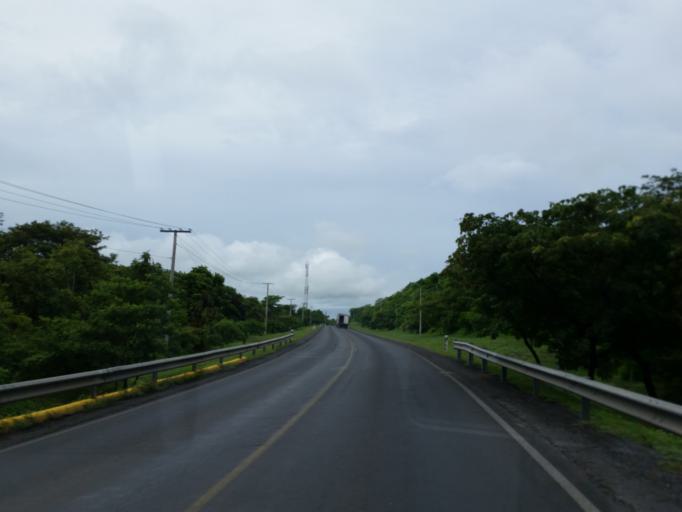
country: NI
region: Leon
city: Nagarote
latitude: 12.2778
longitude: -86.5284
